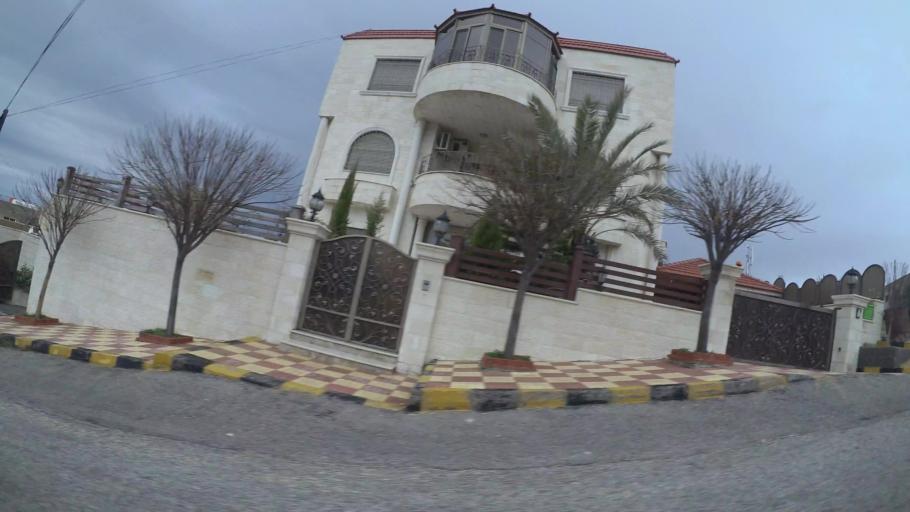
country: JO
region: Amman
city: Al Jubayhah
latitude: 32.0418
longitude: 35.8399
